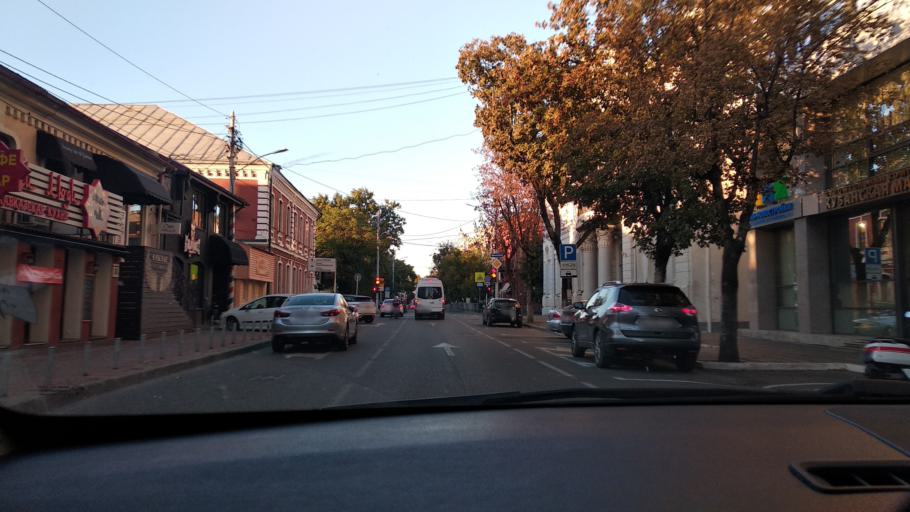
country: RU
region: Krasnodarskiy
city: Krasnodar
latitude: 45.0229
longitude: 38.9719
